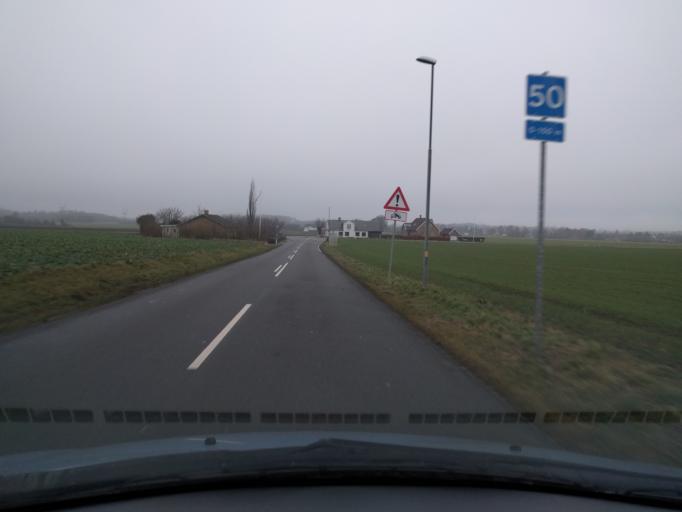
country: DK
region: South Denmark
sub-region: Odense Kommune
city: Bullerup
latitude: 55.3977
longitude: 10.5122
